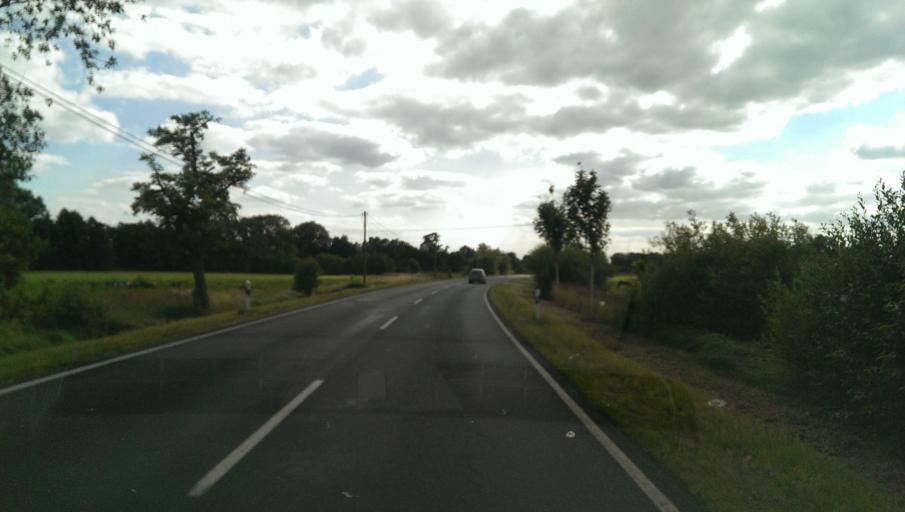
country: DE
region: Saxony-Anhalt
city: Grafenhainichen
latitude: 51.7326
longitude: 12.4756
